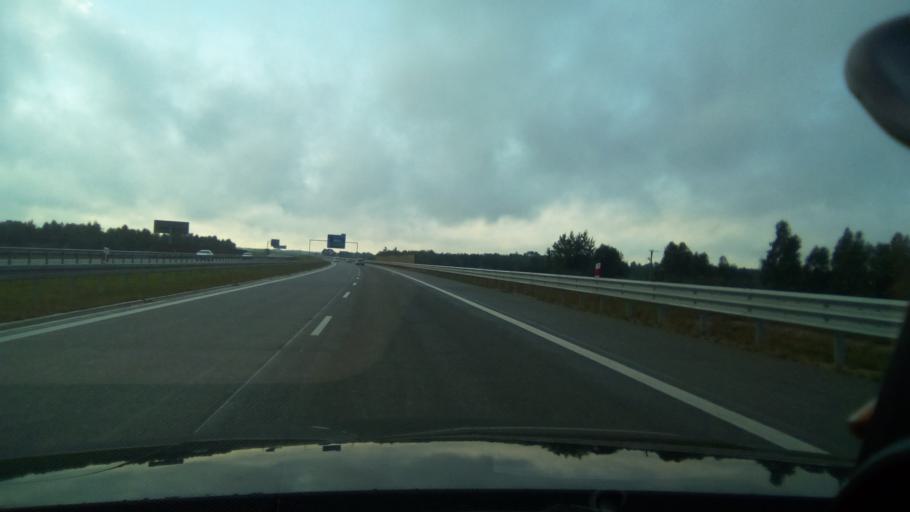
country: PL
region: Silesian Voivodeship
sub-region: Powiat czestochowski
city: Konopiska
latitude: 50.7520
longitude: 19.0304
